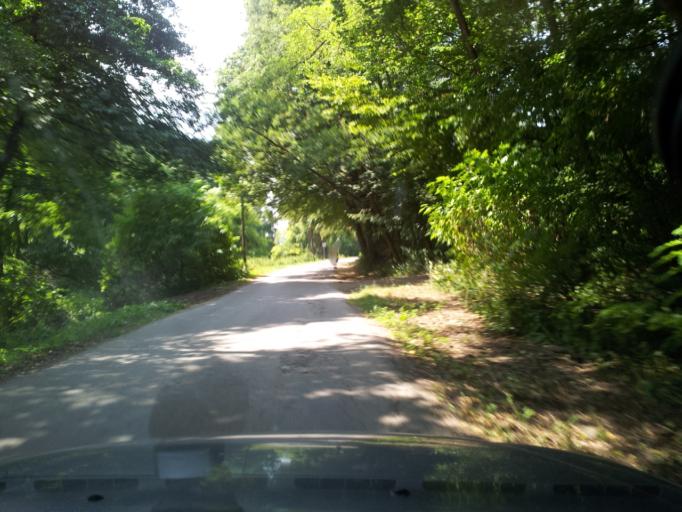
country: SK
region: Trenciansky
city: Nova Dubnica
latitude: 48.9070
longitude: 18.1121
